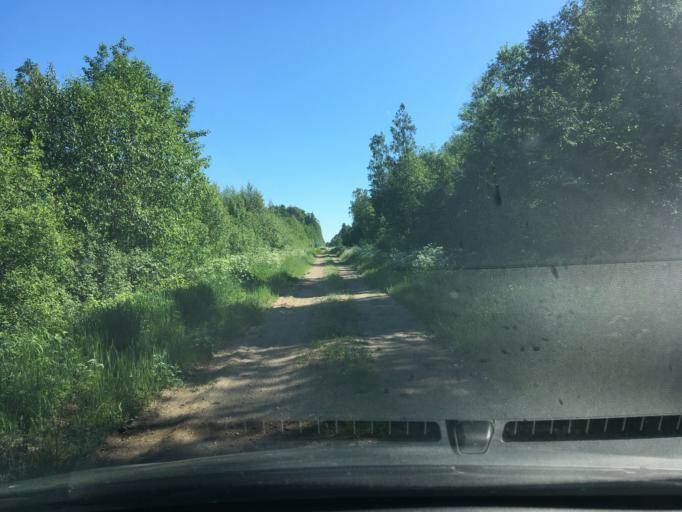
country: EE
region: Laeaene
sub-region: Lihula vald
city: Lihula
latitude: 58.6349
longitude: 23.7515
